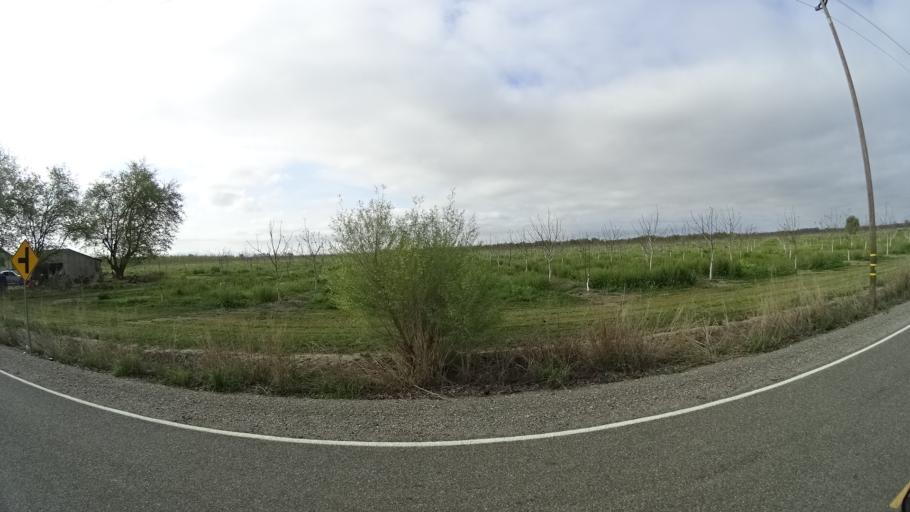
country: US
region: California
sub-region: Colusa County
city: Colusa
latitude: 39.4020
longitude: -121.9686
